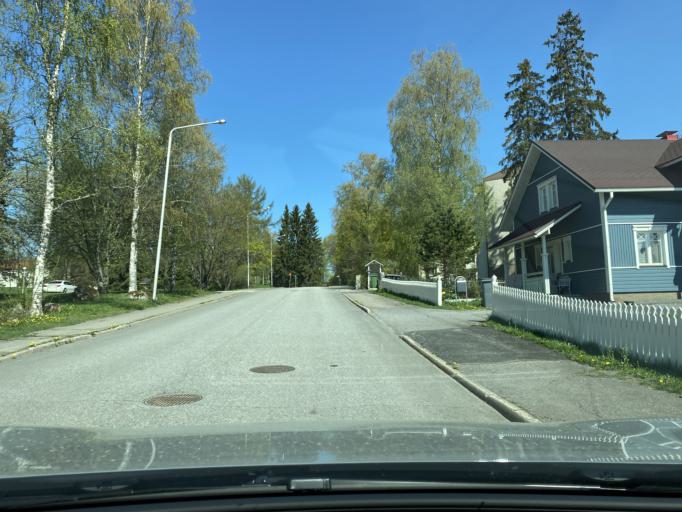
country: FI
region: Pirkanmaa
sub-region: Lounais-Pirkanmaa
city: Vammala
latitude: 61.3476
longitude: 22.8960
